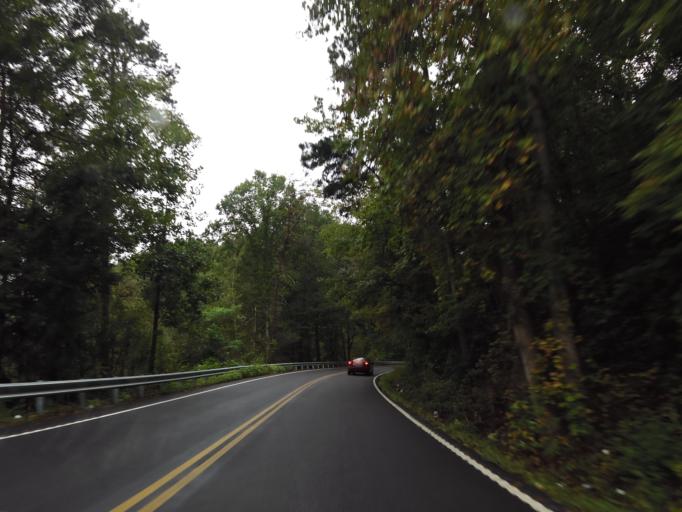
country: US
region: Tennessee
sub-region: Bradley County
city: Cleveland
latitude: 35.1715
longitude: -84.9959
